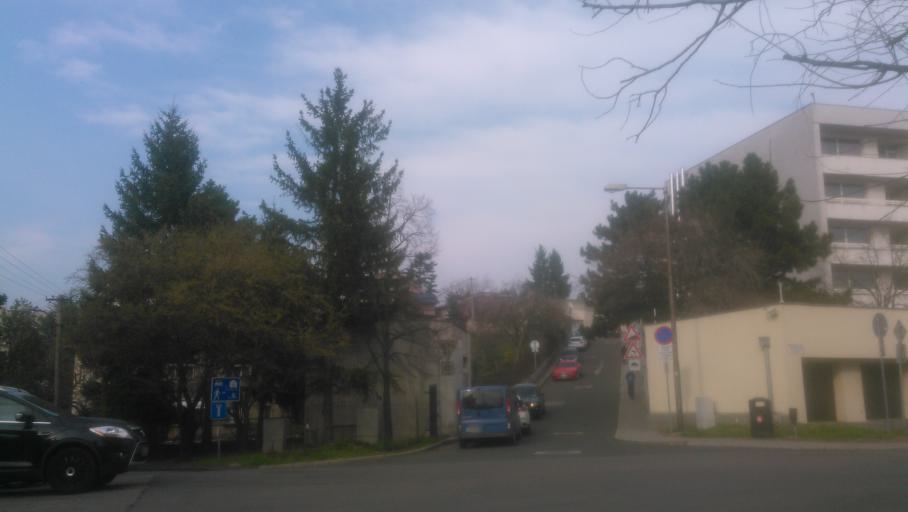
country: SK
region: Bratislavsky
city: Bratislava
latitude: 48.1486
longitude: 17.0860
